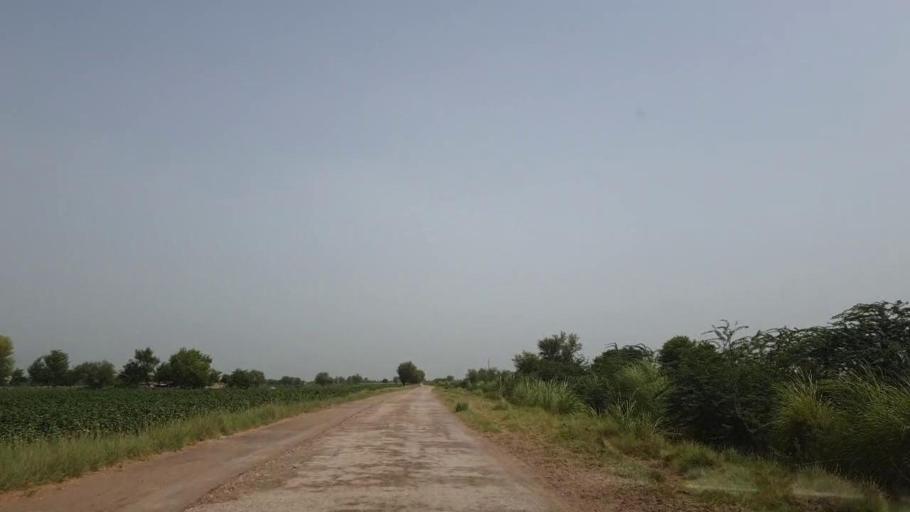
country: PK
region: Sindh
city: Sakrand
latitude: 26.1311
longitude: 68.3642
